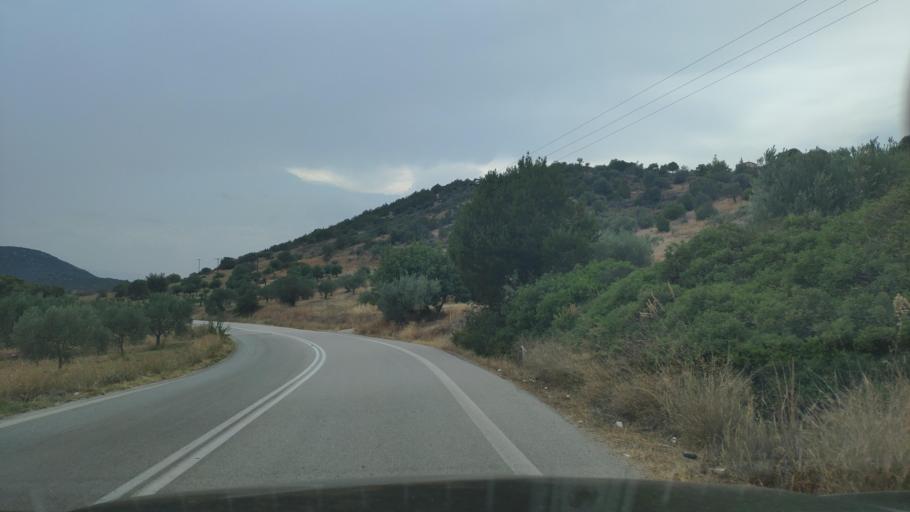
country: GR
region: Peloponnese
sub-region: Nomos Argolidos
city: Didyma
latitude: 37.4313
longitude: 23.1641
